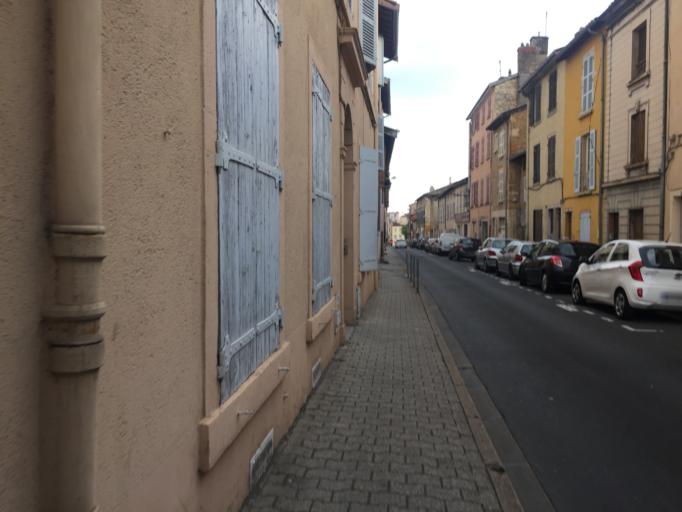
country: FR
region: Rhone-Alpes
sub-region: Departement du Rhone
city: Villefranche-sur-Saone
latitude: 45.9925
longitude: 4.7180
